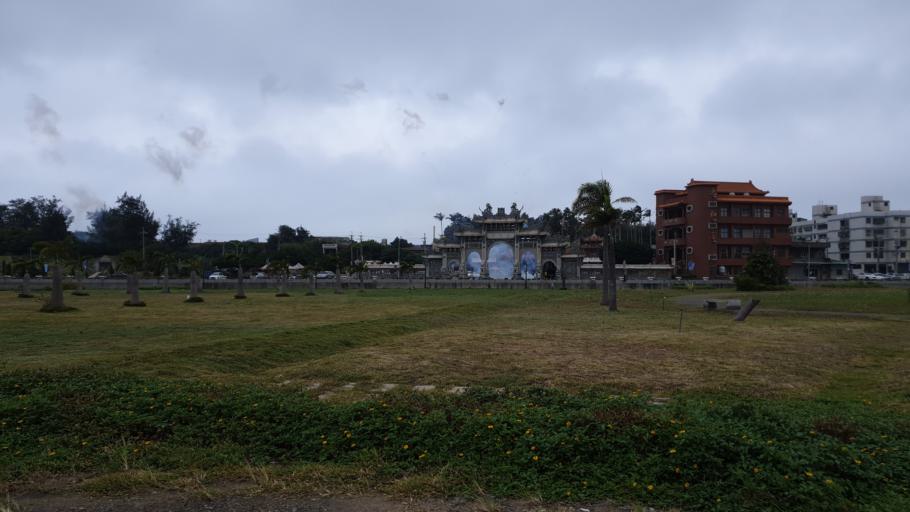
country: TW
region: Taiwan
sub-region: Hsinchu
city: Zhubei
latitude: 24.9090
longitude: 120.9775
